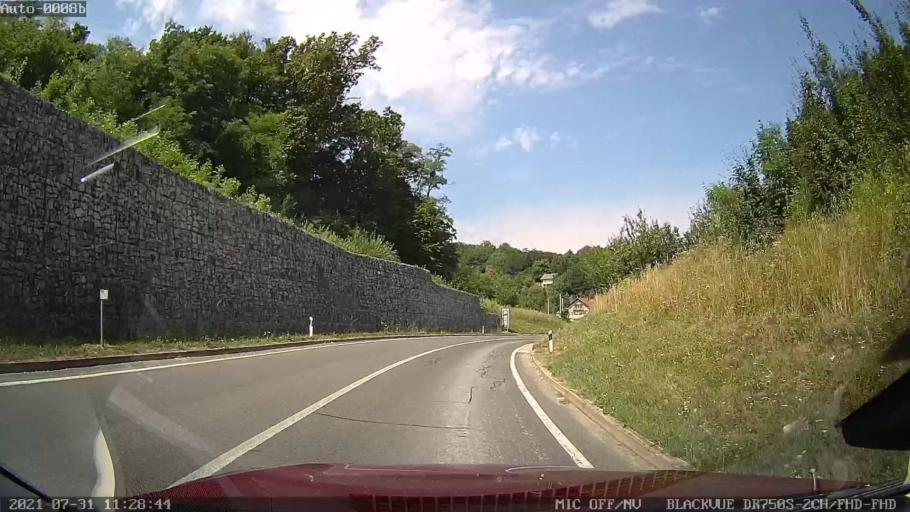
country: HR
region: Varazdinska
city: Ljubescica
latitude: 46.2025
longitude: 16.4221
